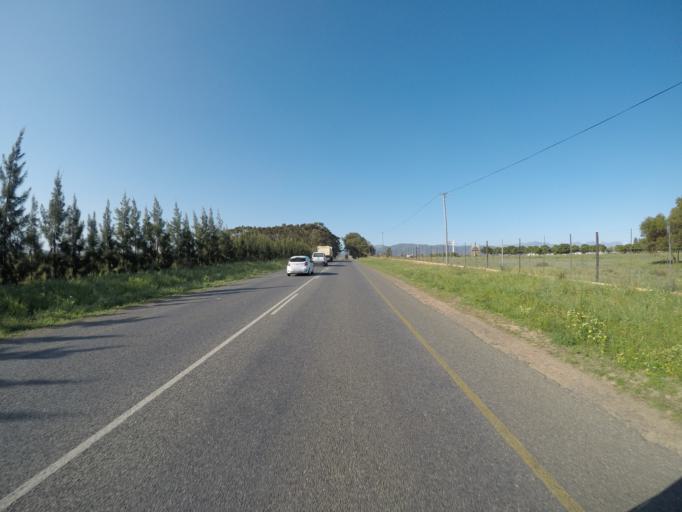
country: ZA
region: Western Cape
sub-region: City of Cape Town
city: Kraaifontein
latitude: -33.7603
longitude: 18.8081
